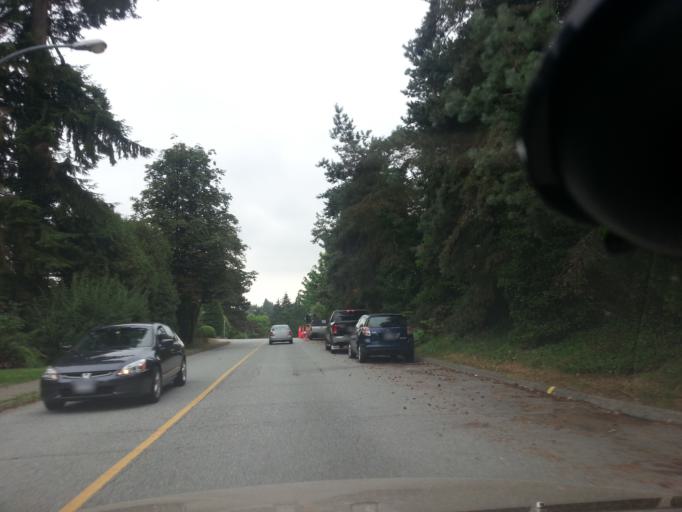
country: CA
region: British Columbia
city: Port Moody
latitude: 49.2841
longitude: -122.8767
